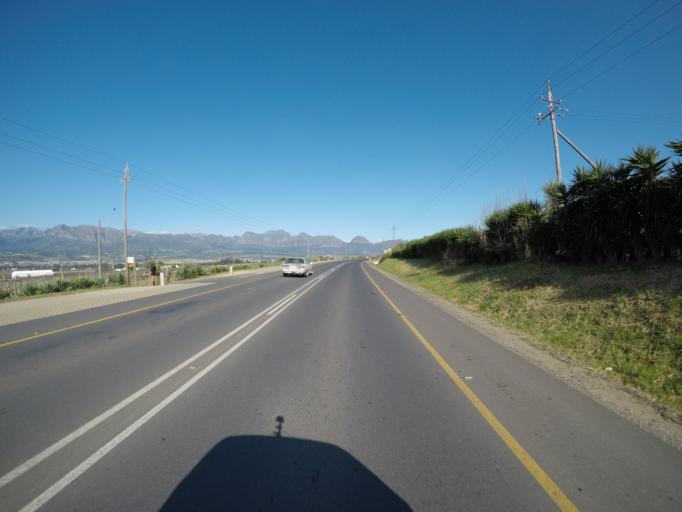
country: ZA
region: Western Cape
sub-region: Cape Winelands District Municipality
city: Noorder-Paarl
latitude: -33.6810
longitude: 18.9451
